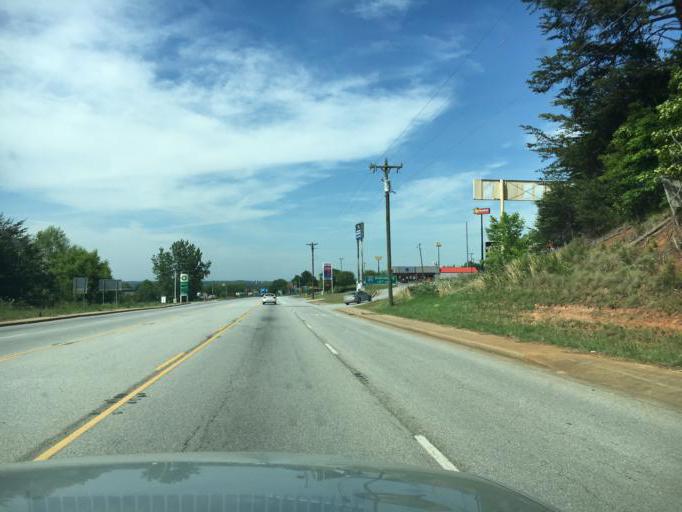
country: US
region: South Carolina
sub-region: Cherokee County
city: Blacksburg
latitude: 35.1377
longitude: -81.5091
